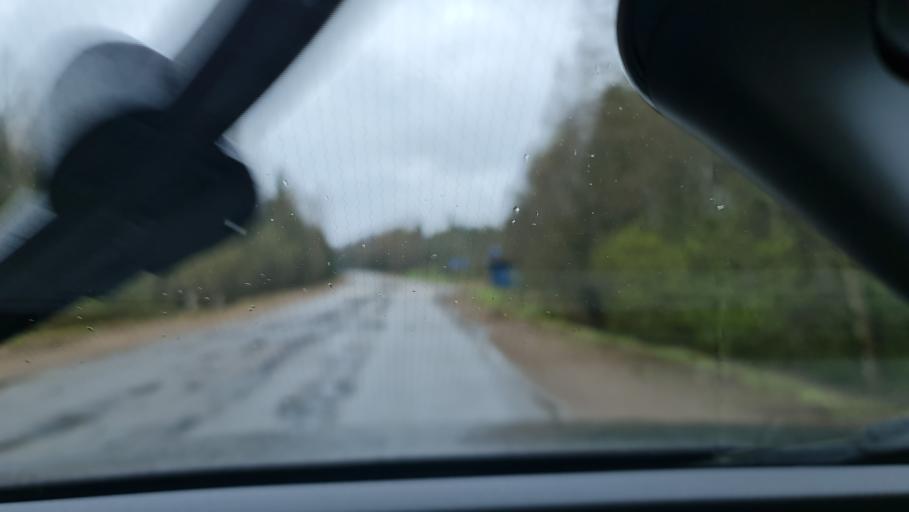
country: RU
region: Novgorod
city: Kresttsy
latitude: 58.0340
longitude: 32.8289
